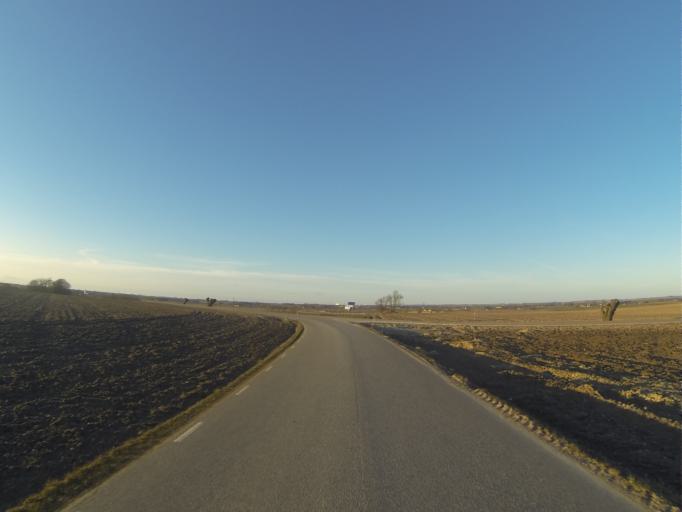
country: SE
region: Skane
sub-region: Staffanstorps Kommun
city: Staffanstorp
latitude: 55.6049
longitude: 13.1837
